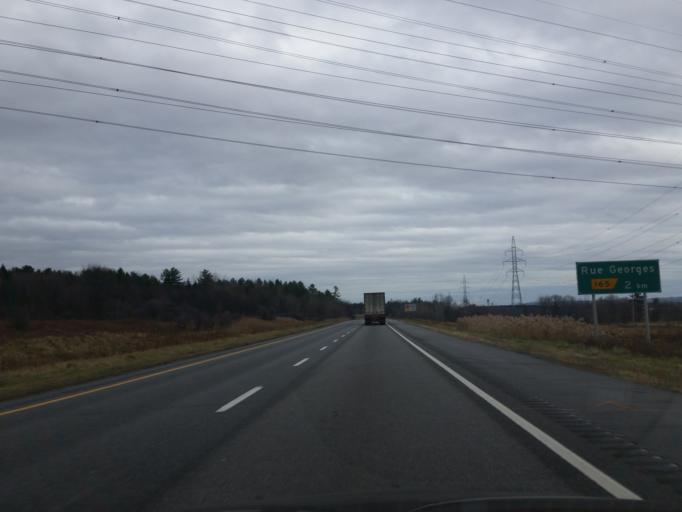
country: CA
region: Ontario
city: Clarence-Rockland
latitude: 45.5416
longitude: -75.4631
